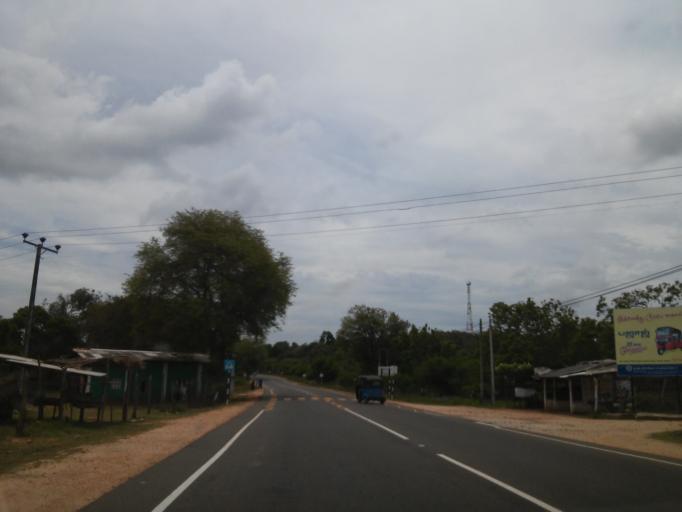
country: LK
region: Eastern Province
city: Trincomalee
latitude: 8.5407
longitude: 81.1175
